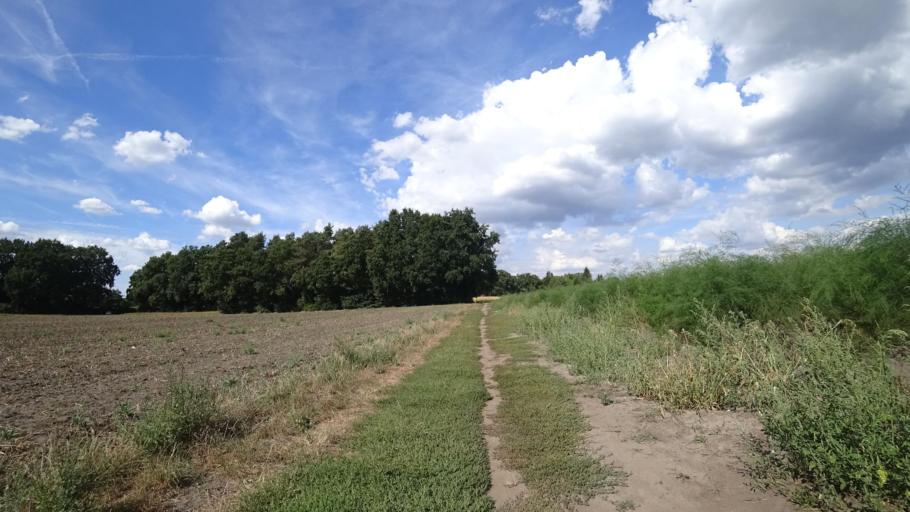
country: DE
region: North Rhine-Westphalia
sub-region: Regierungsbezirk Detmold
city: Verl
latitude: 51.9390
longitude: 8.4963
